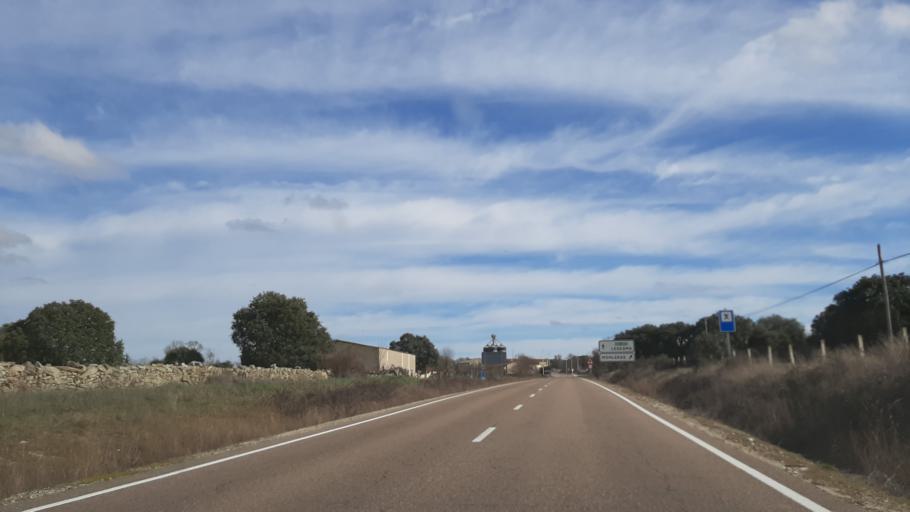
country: ES
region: Castille and Leon
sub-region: Provincia de Salamanca
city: Monleras
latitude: 41.1845
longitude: -6.2296
